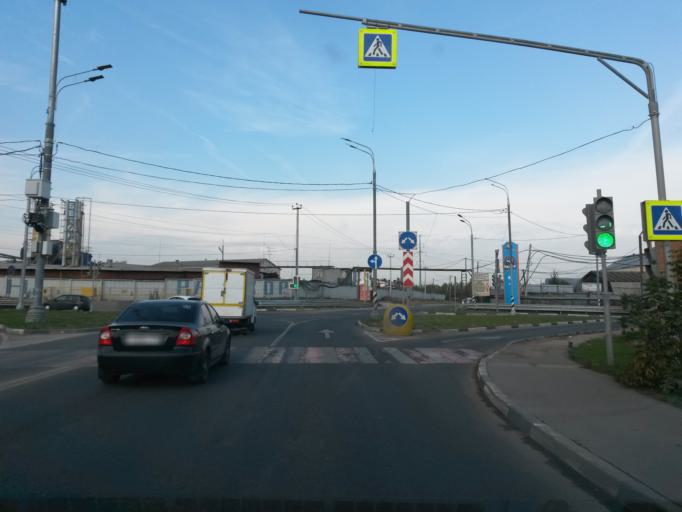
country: RU
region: Moskovskaya
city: Mosrentgen
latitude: 55.6068
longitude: 37.4593
